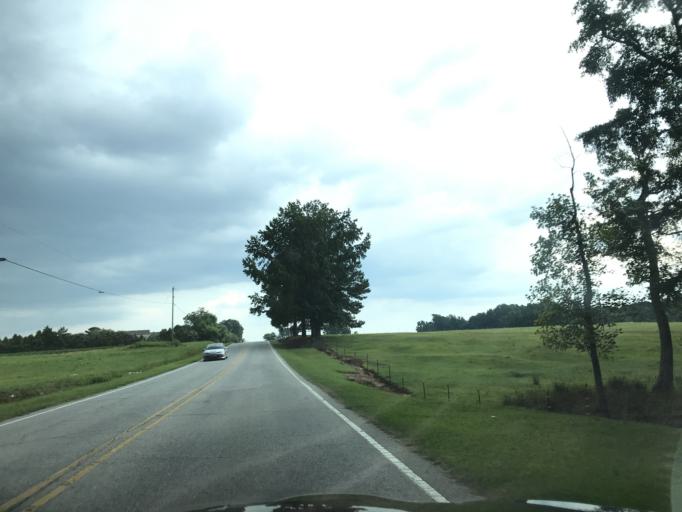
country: US
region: North Carolina
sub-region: Johnston County
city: Four Oaks
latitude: 35.5130
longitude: -78.4852
